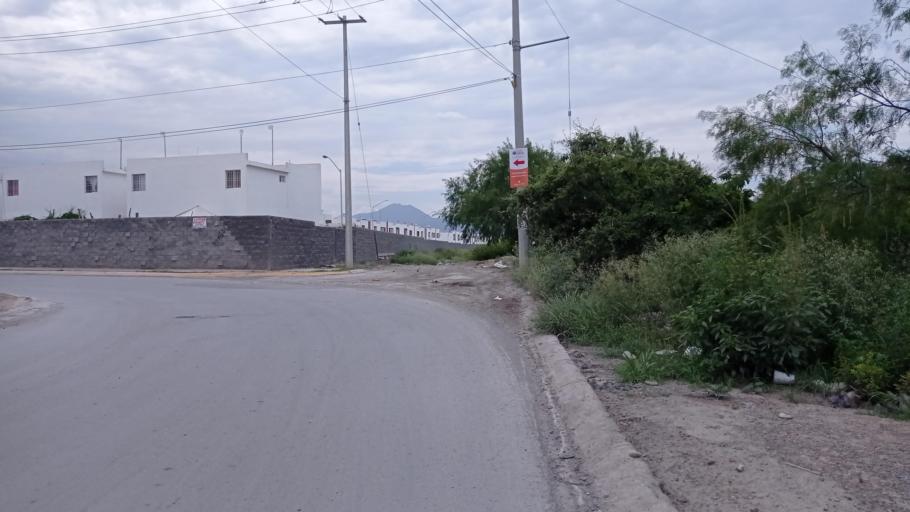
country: MX
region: Nuevo Leon
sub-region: Salinas Victoria
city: Simeprodeso (Colectivo Nuevo)
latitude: 25.8772
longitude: -100.3149
